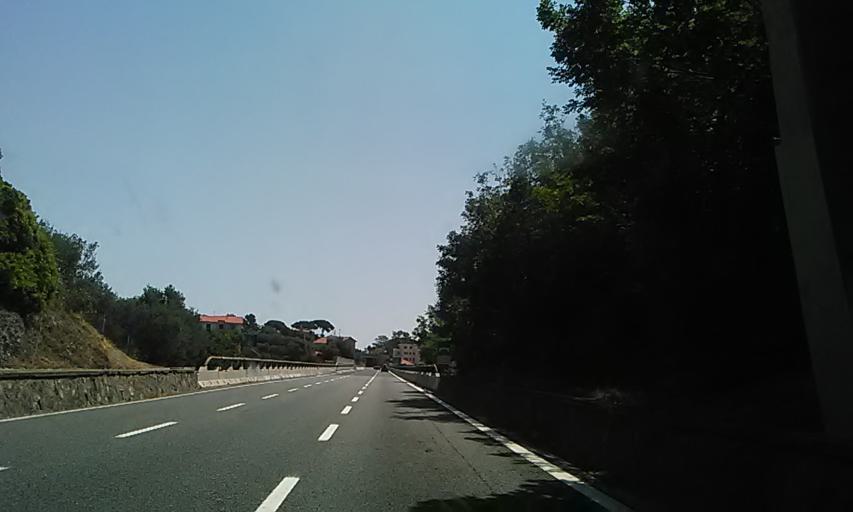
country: IT
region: Liguria
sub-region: Provincia di Savona
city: Celle Ligure
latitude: 44.3478
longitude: 8.5497
